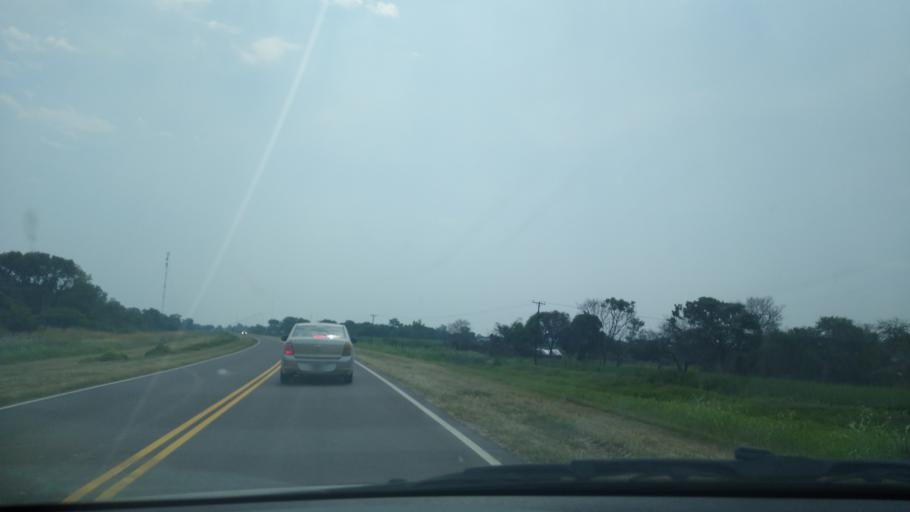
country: AR
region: Chaco
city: La Eduvigis
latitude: -26.8400
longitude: -59.0563
